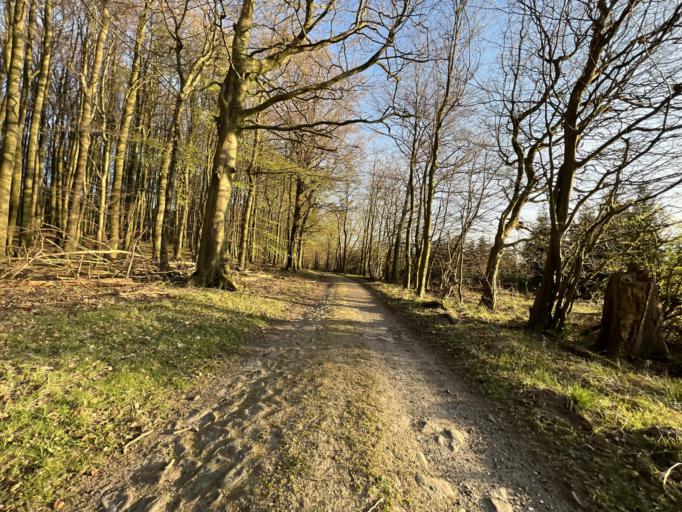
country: DE
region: Mecklenburg-Vorpommern
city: Sassnitz
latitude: 54.5357
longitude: 13.6534
